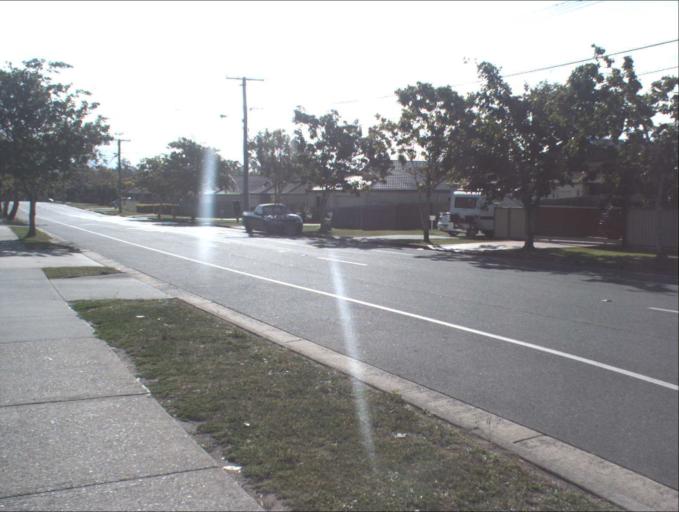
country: AU
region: Queensland
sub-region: Logan
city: Waterford West
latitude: -27.6822
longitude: 153.1167
